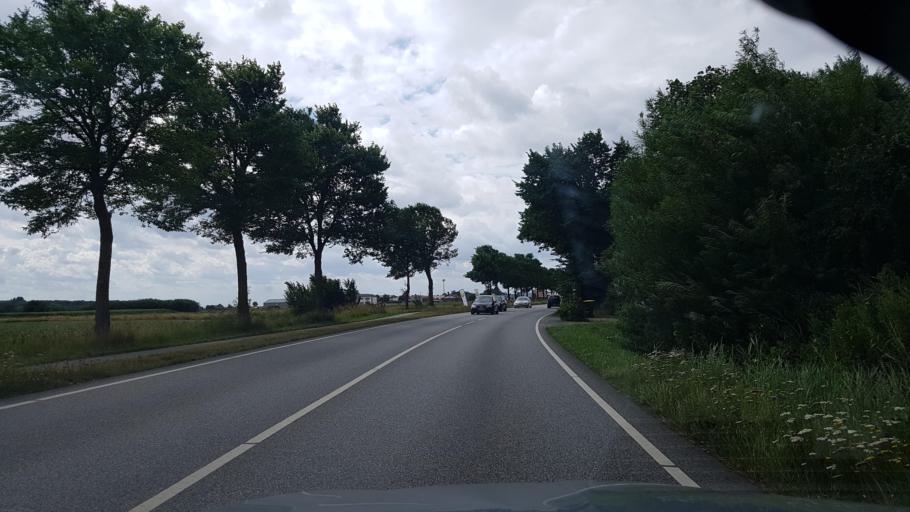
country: DE
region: Schleswig-Holstein
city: Oesterdeichstrich
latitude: 54.1455
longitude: 8.8771
